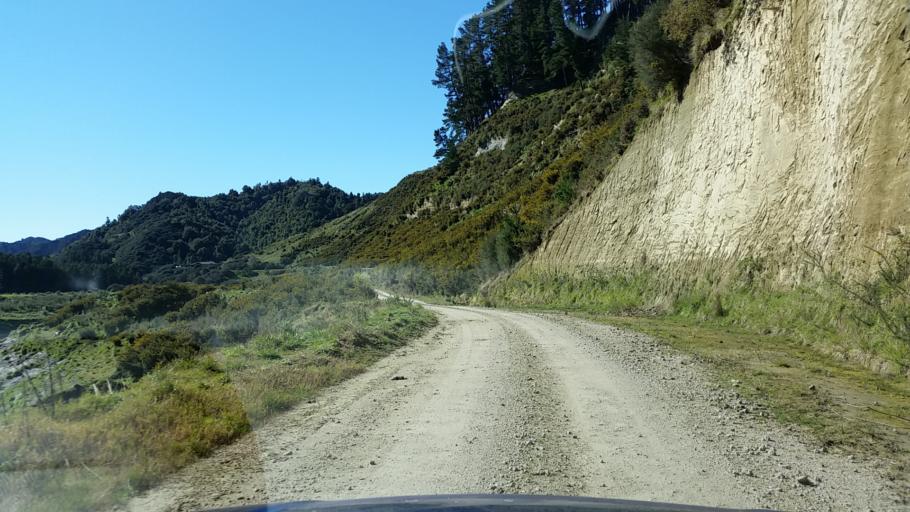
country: NZ
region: Manawatu-Wanganui
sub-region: Wanganui District
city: Wanganui
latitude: -39.6679
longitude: 174.8715
